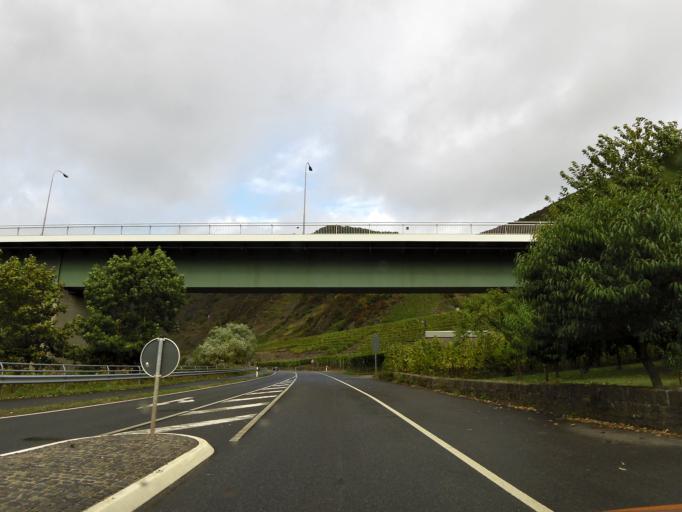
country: DE
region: Rheinland-Pfalz
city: Bruttig-Fankel
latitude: 50.1375
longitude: 7.2365
